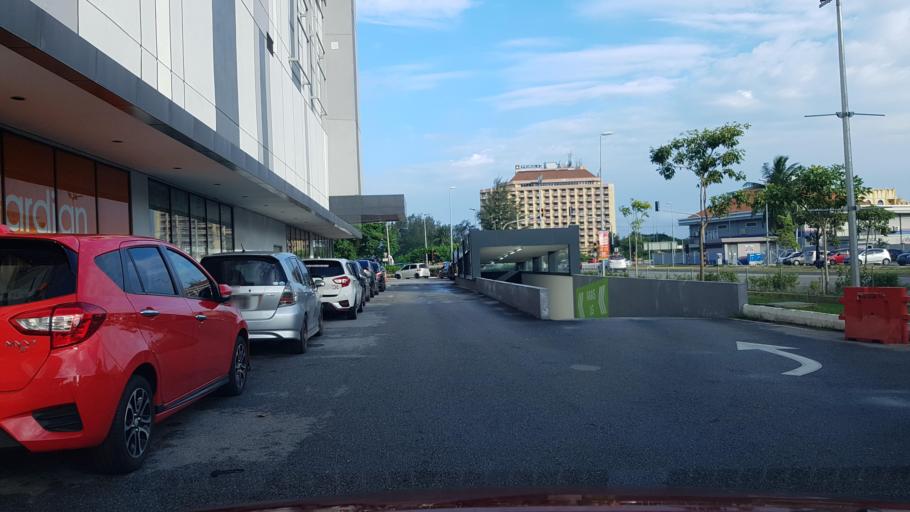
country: MY
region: Terengganu
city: Kuala Terengganu
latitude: 5.3330
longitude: 103.1497
